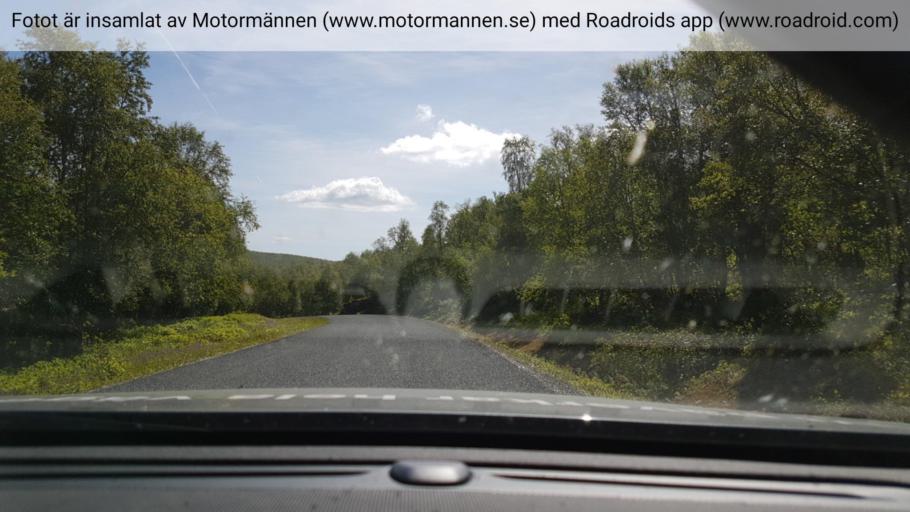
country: NO
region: Nordland
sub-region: Hattfjelldal
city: Hattfjelldal
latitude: 65.4220
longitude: 14.9097
